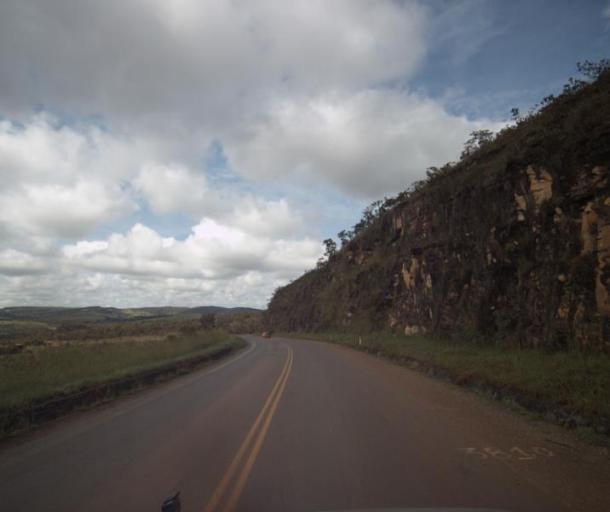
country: BR
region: Goias
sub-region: Pirenopolis
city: Pirenopolis
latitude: -15.8440
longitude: -48.7704
